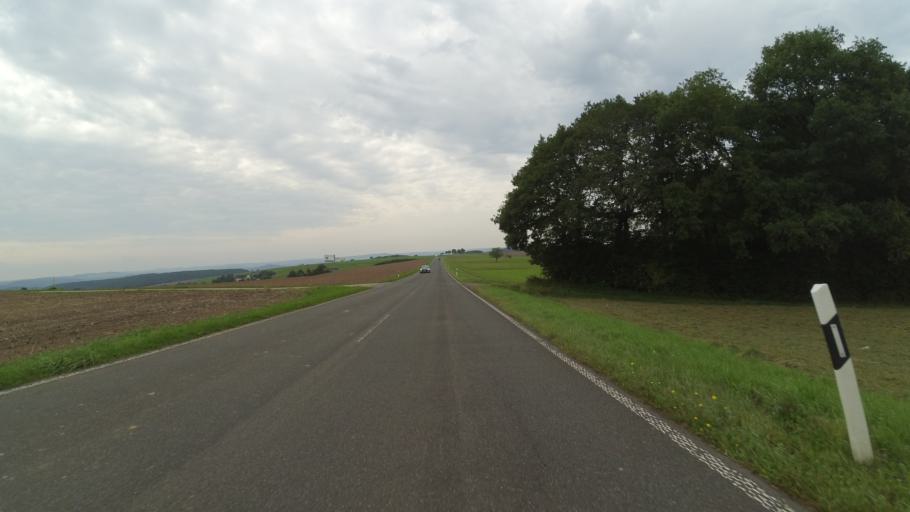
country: DE
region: Rheinland-Pfalz
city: Irsch
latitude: 49.5992
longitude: 6.6408
